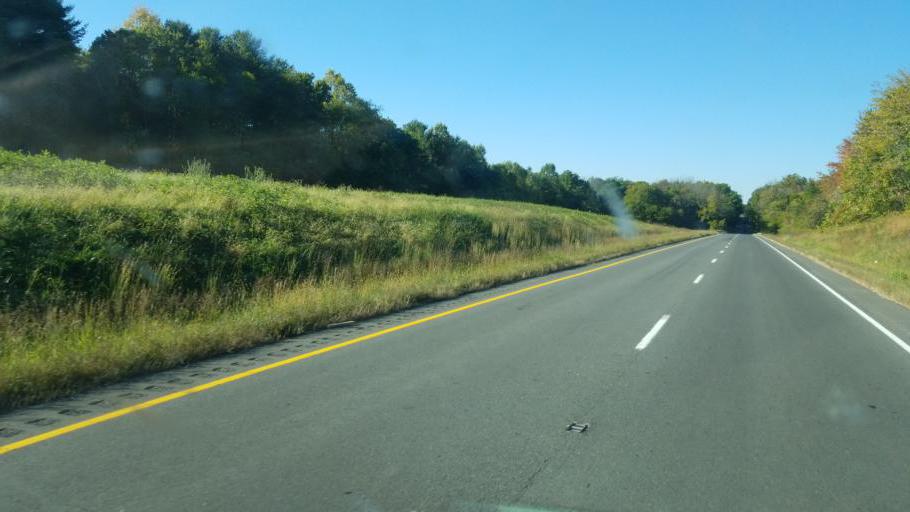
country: US
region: Virginia
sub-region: Culpeper County
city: Culpeper
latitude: 38.4657
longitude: -77.9616
